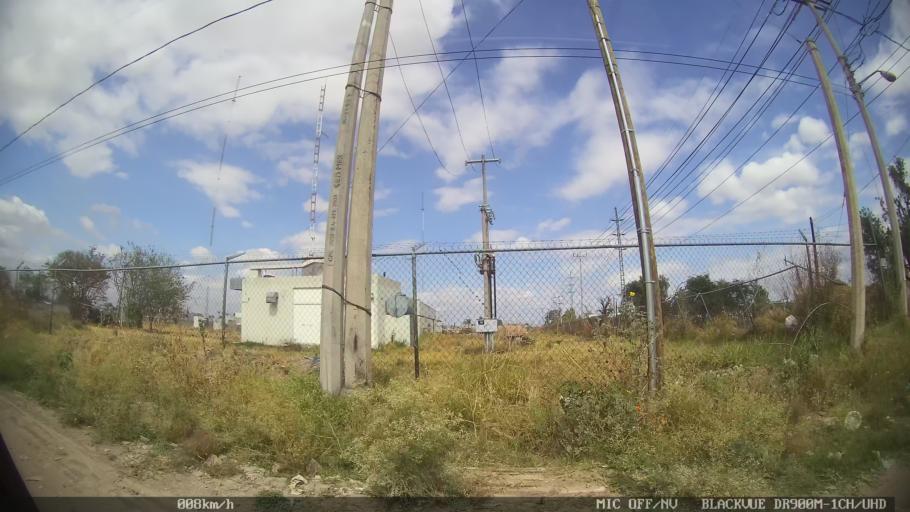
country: MX
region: Jalisco
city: Tonala
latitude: 20.6659
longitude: -103.2477
